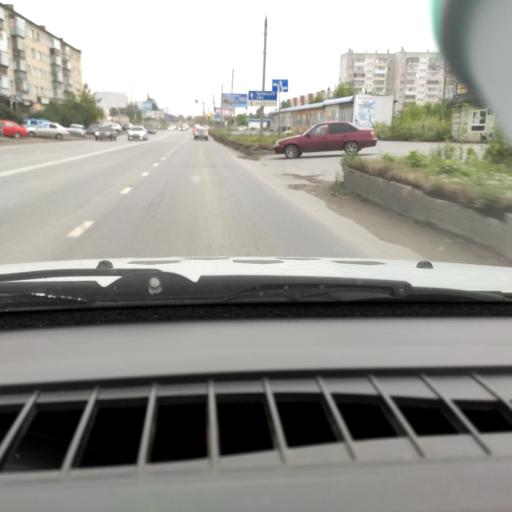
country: RU
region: Chelyabinsk
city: Miass
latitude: 55.0469
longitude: 60.1037
